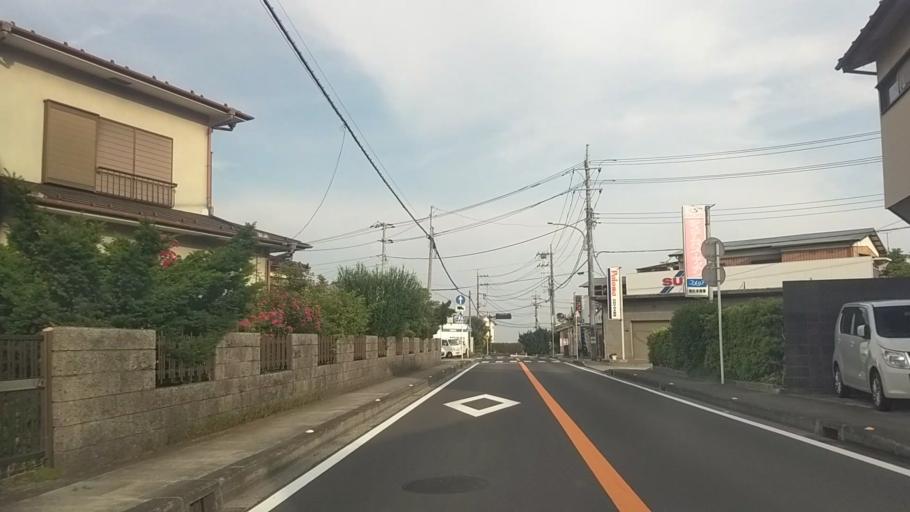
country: JP
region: Kanagawa
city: Odawara
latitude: 35.3521
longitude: 139.0933
